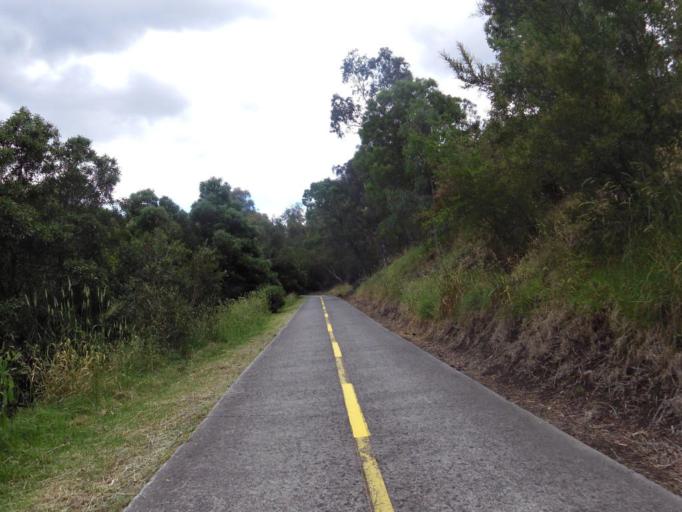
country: AU
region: Victoria
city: Heidelberg West
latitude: -37.7475
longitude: 145.0359
